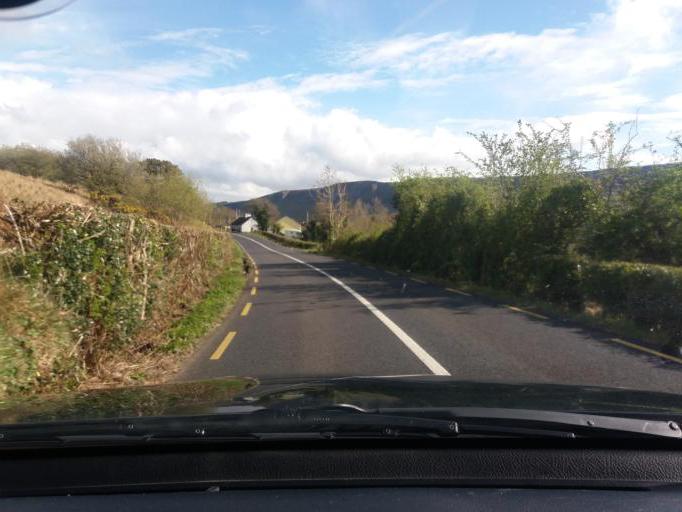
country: IE
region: Connaught
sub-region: County Leitrim
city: Kinlough
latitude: 54.3893
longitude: -8.3021
